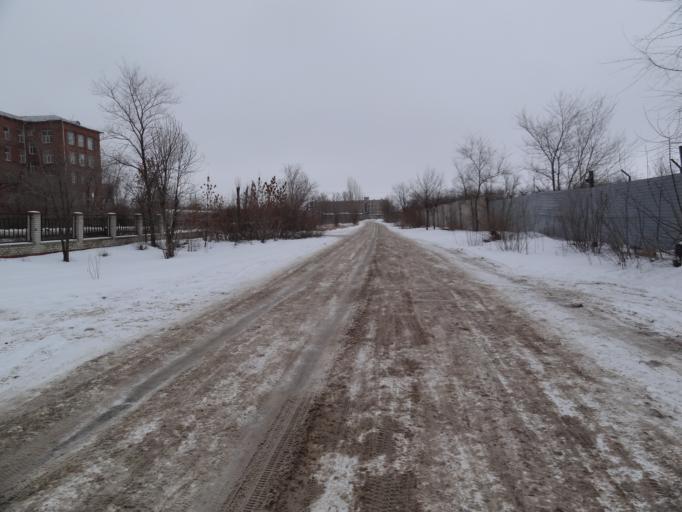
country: RU
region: Saratov
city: Engel's
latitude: 51.4707
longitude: 46.1560
